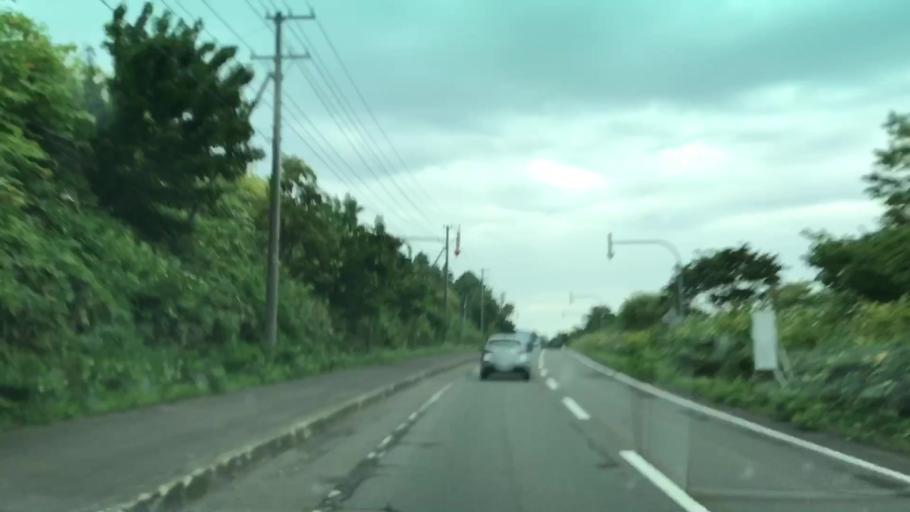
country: JP
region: Hokkaido
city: Iwanai
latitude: 42.7568
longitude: 140.2675
